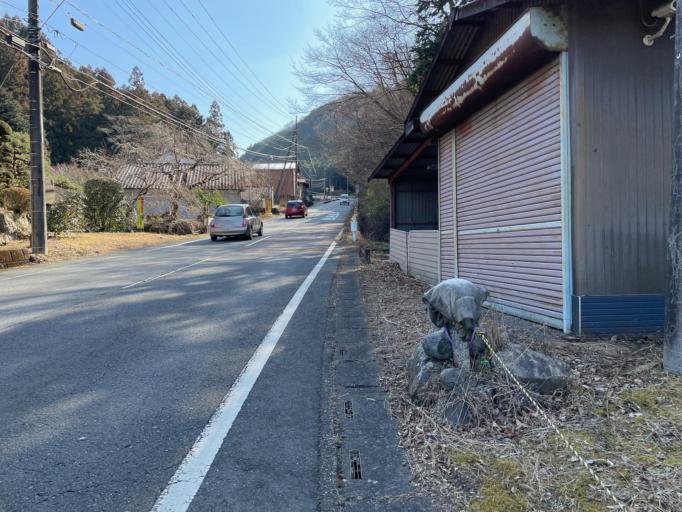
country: JP
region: Tokyo
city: Ome
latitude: 35.8608
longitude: 139.2383
